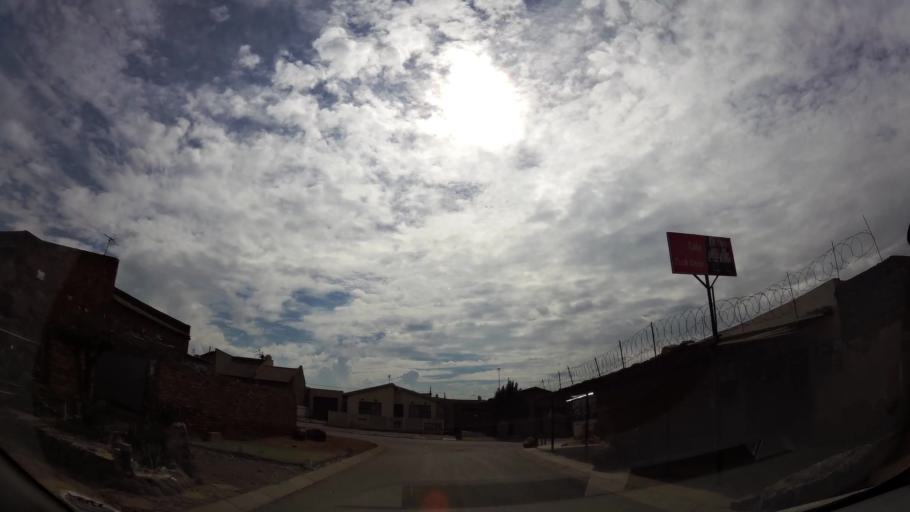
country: ZA
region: Gauteng
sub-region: Ekurhuleni Metropolitan Municipality
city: Germiston
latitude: -26.3787
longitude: 28.1675
